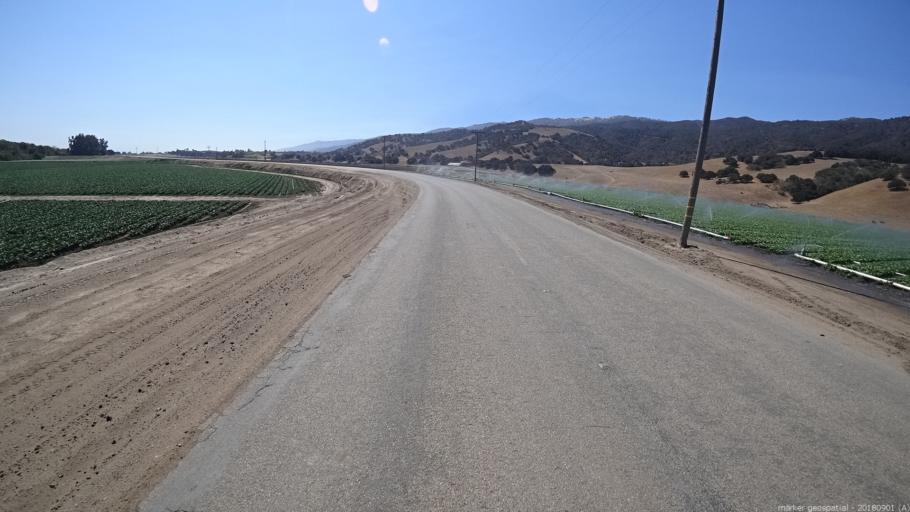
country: US
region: California
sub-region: Monterey County
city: Chualar
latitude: 36.5359
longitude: -121.5416
